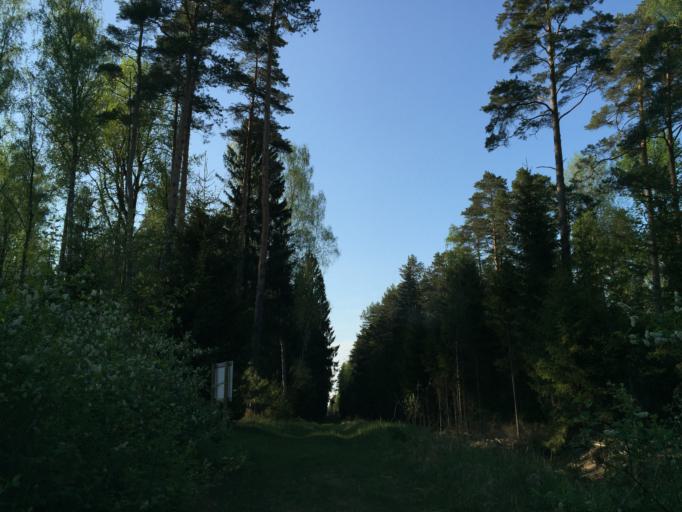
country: LV
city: Tireli
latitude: 56.8380
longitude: 23.7073
